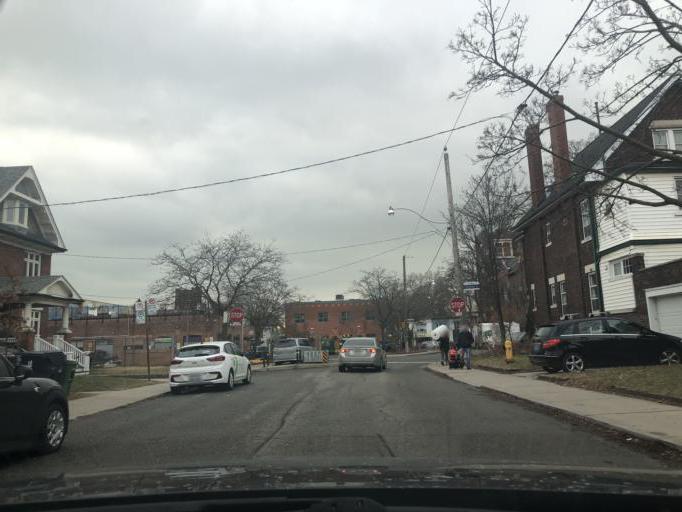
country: CA
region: Ontario
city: Toronto
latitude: 43.6791
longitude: -79.3547
